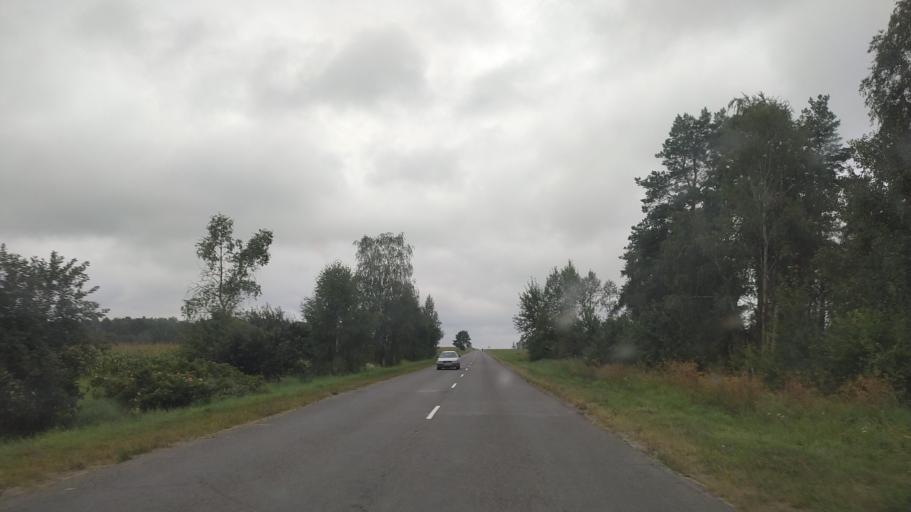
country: BY
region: Brest
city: Byaroza
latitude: 52.5611
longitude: 24.9085
